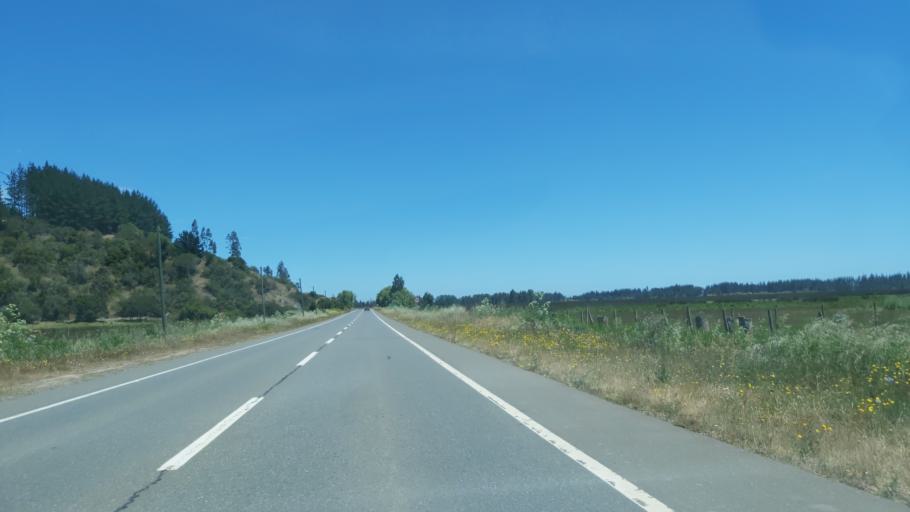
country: CL
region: Maule
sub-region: Provincia de Talca
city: Constitucion
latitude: -35.1544
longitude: -72.2367
